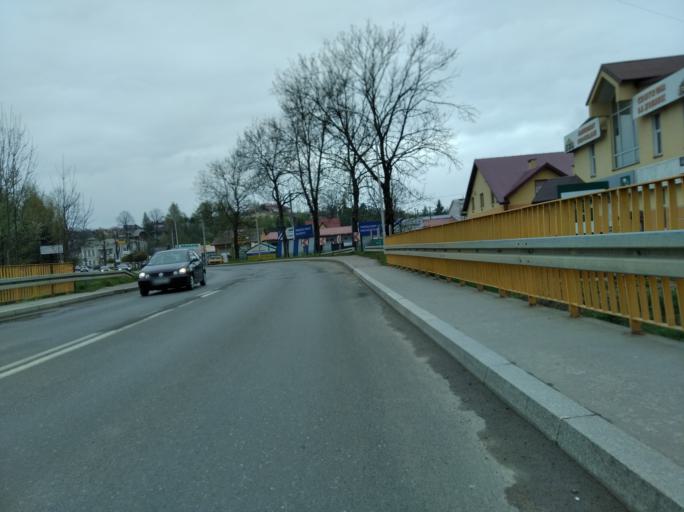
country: PL
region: Subcarpathian Voivodeship
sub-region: Powiat brzozowski
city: Brzozow
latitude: 49.7013
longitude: 22.0197
